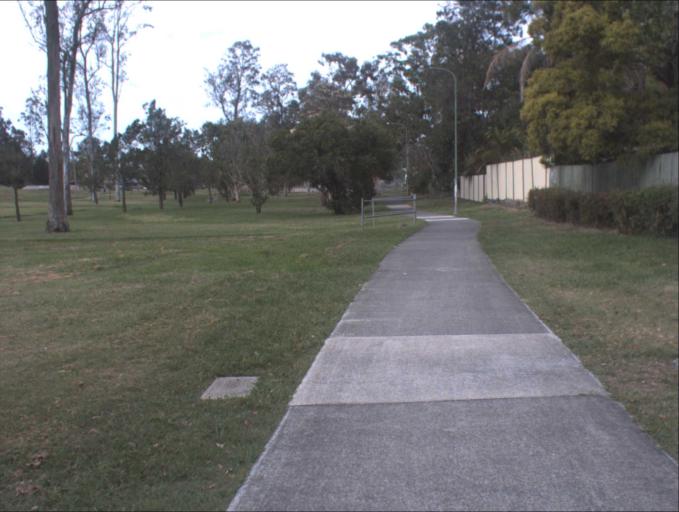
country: AU
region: Queensland
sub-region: Logan
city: Logan City
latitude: -27.6340
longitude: 153.1166
